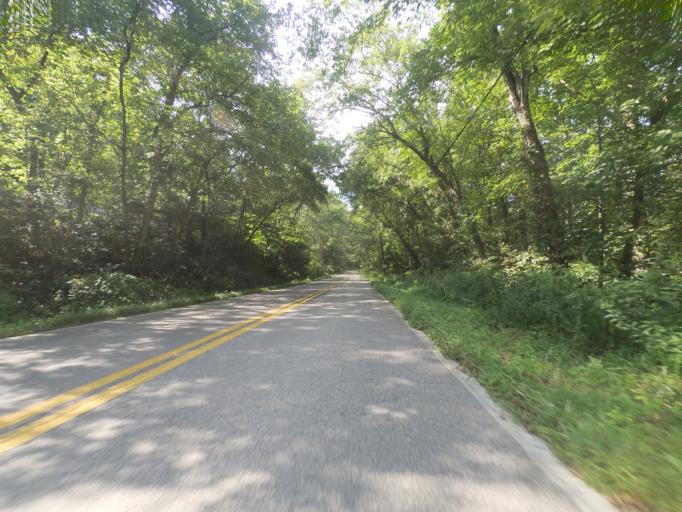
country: US
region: West Virginia
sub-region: Wayne County
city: Ceredo
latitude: 38.3779
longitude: -82.5604
